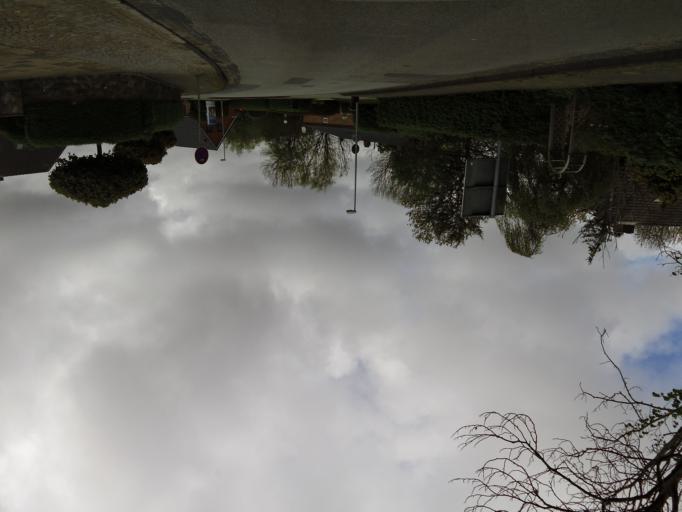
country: DE
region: Schleswig-Holstein
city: Niebull
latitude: 54.7777
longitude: 8.8141
